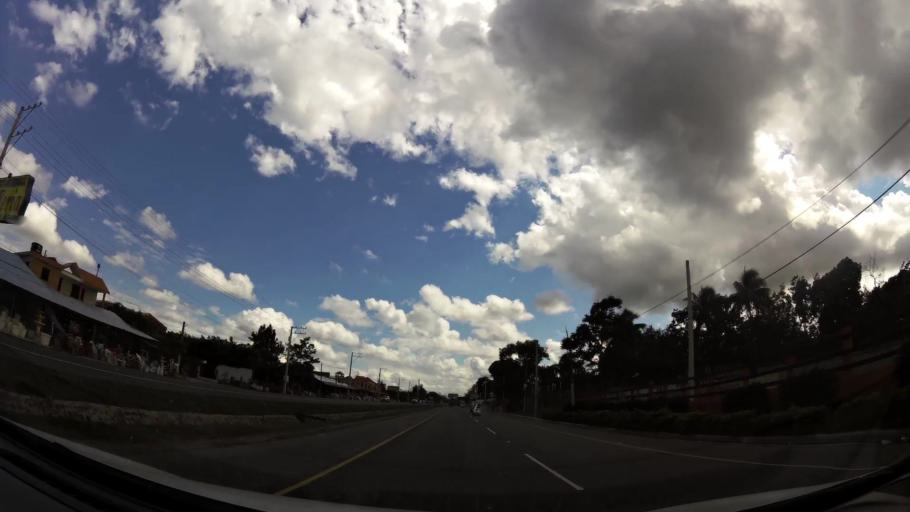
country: DO
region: La Vega
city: Rio Verde Arriba
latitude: 19.3565
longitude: -70.6013
